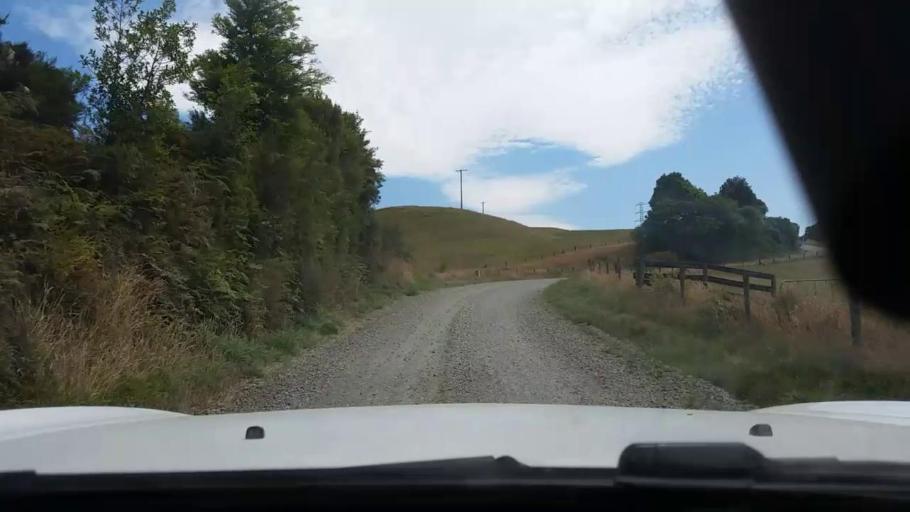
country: NZ
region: Bay of Plenty
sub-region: Rotorua District
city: Rotorua
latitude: -37.9900
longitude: 176.1777
